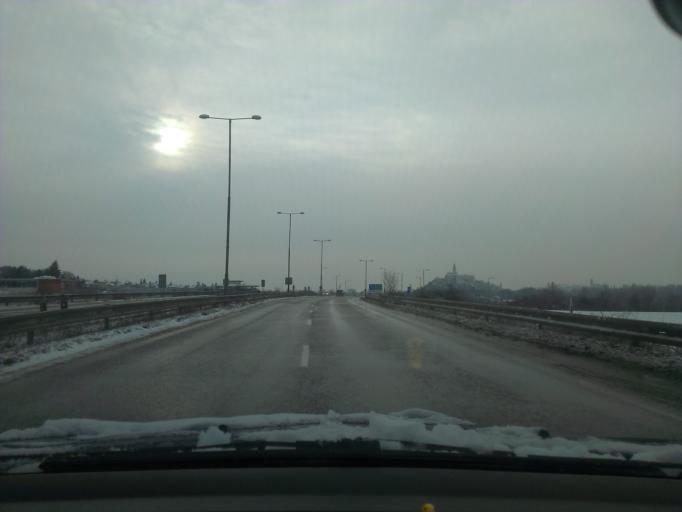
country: SK
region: Nitriansky
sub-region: Okres Nitra
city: Nitra
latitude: 48.3318
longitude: 18.0787
